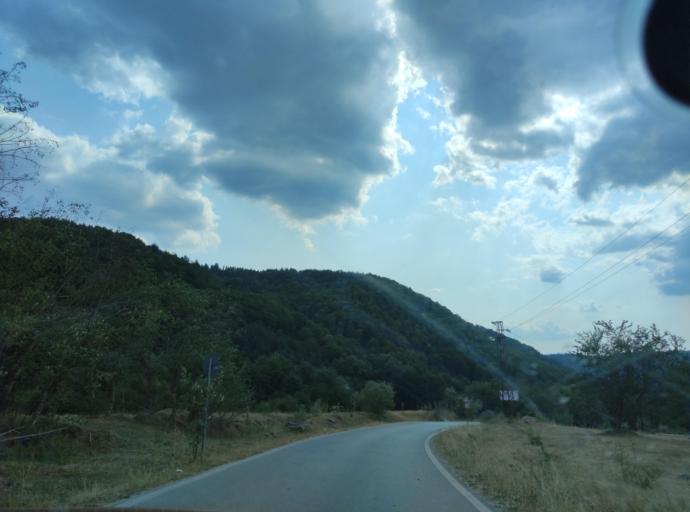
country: BG
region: Blagoevgrad
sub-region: Obshtina Belitsa
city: Belitsa
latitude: 42.0104
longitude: 23.5662
